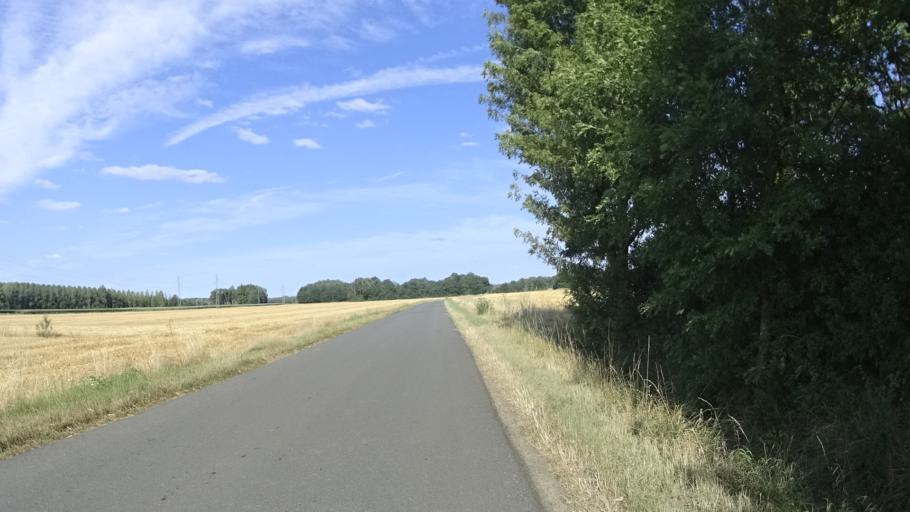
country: FR
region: Centre
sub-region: Departement du Loir-et-Cher
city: Onzain
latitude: 47.4873
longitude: 1.1571
